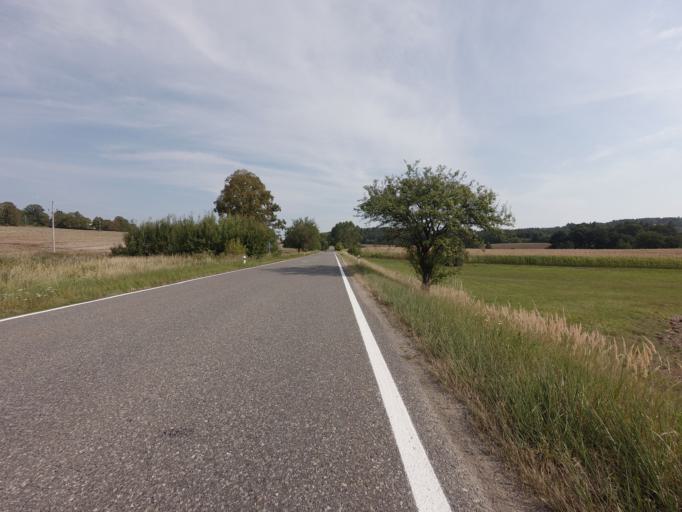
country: CZ
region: Jihocesky
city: Milevsko
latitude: 49.4962
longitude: 14.3615
